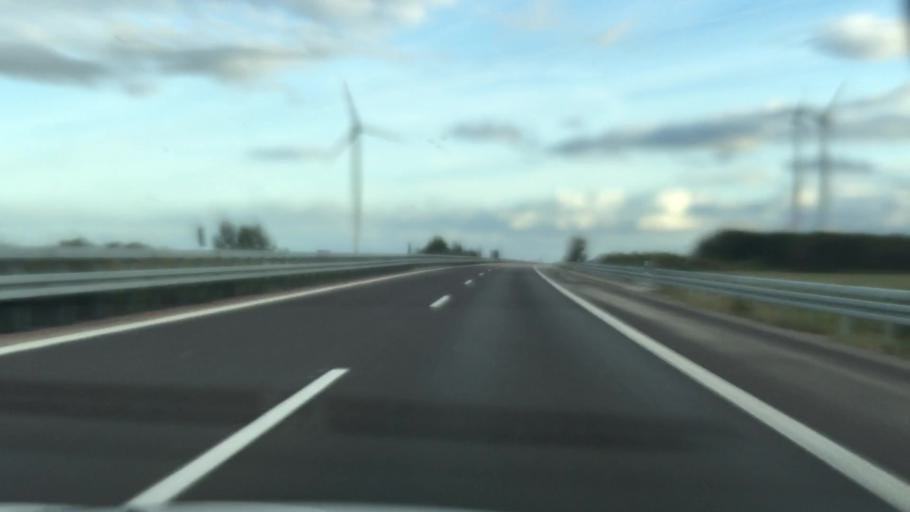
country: DE
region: Saxony-Anhalt
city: Nauendorf
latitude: 51.6293
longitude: 11.8617
